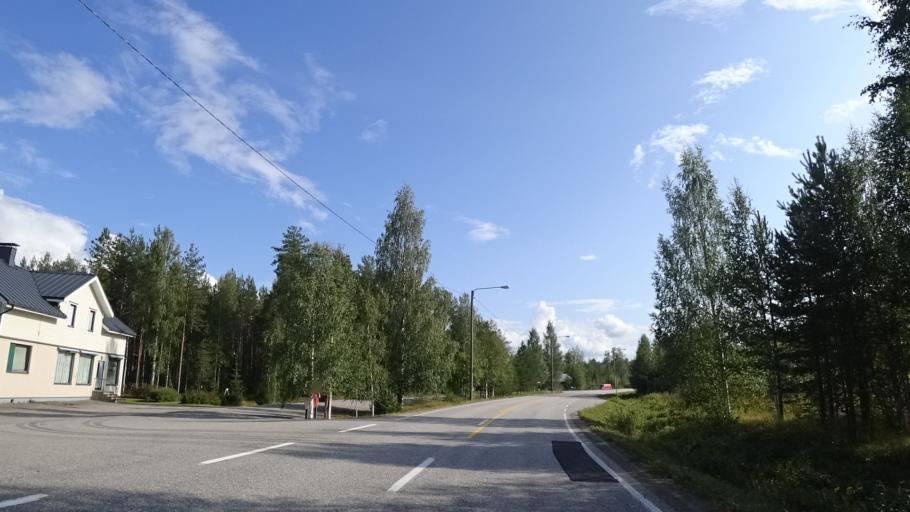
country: FI
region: North Karelia
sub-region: Pielisen Karjala
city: Lieksa
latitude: 63.4204
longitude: 30.1047
